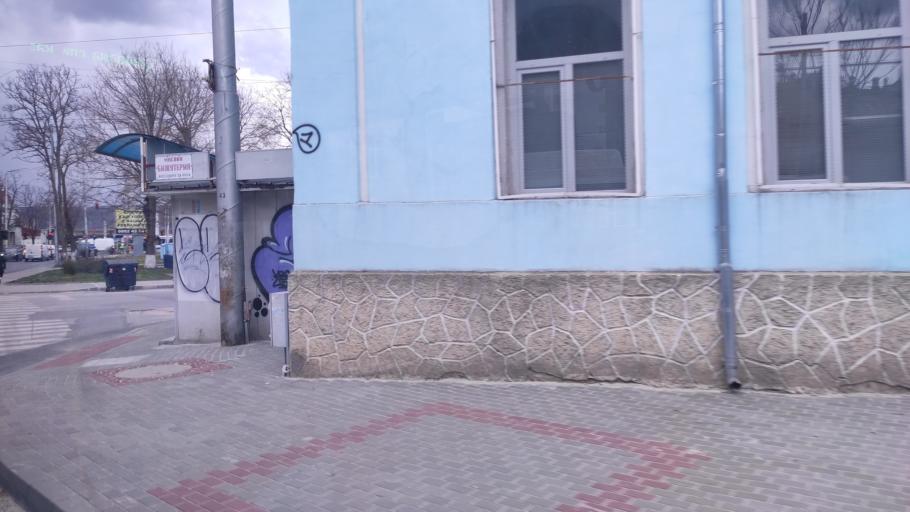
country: BG
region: Varna
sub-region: Obshtina Varna
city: Varna
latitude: 43.2000
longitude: 27.9115
